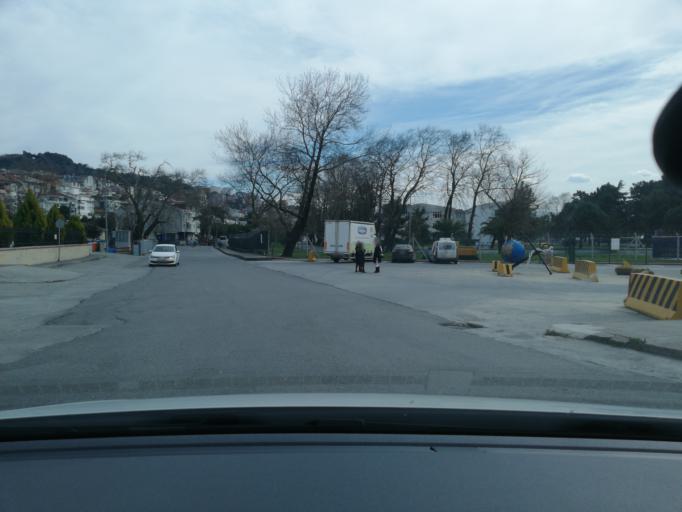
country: TR
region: Zonguldak
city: Eregli
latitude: 41.2909
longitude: 31.4066
